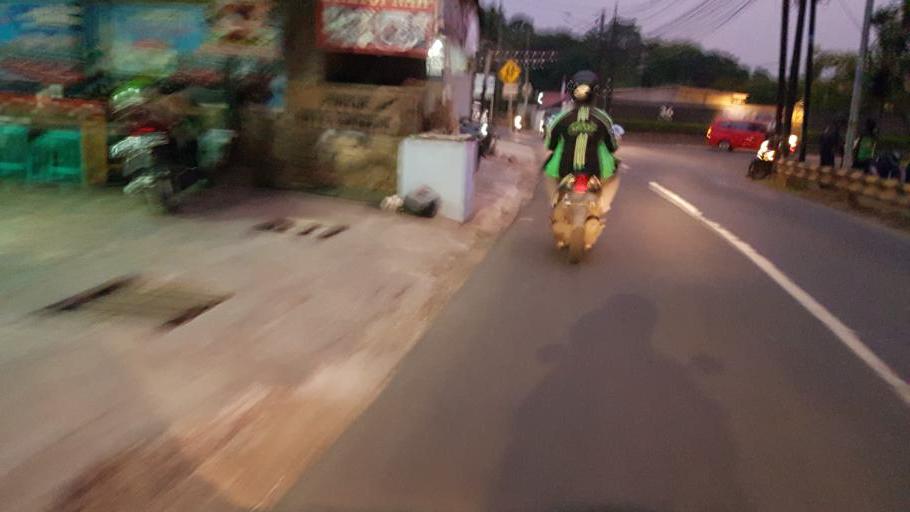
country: ID
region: Jakarta Raya
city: Jakarta
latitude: -6.2972
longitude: 106.8262
